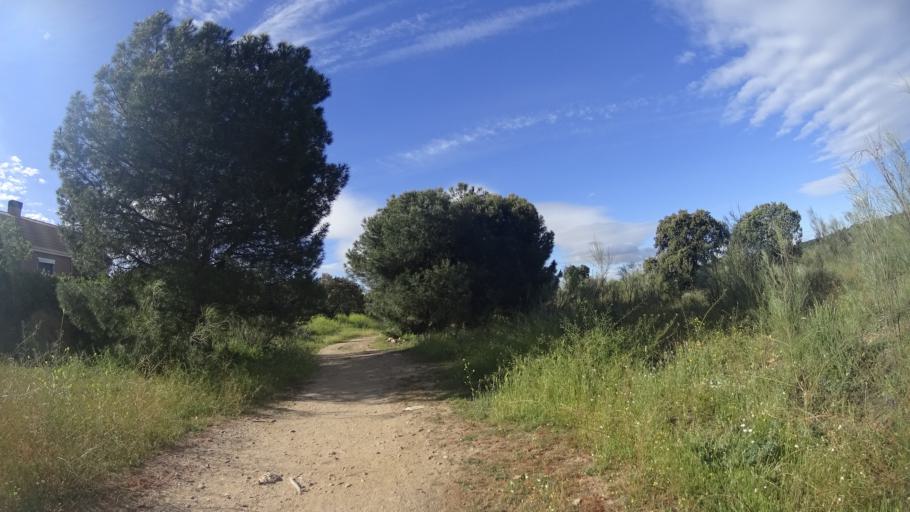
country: ES
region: Madrid
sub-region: Provincia de Madrid
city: Villanueva del Pardillo
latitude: 40.5246
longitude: -3.9357
